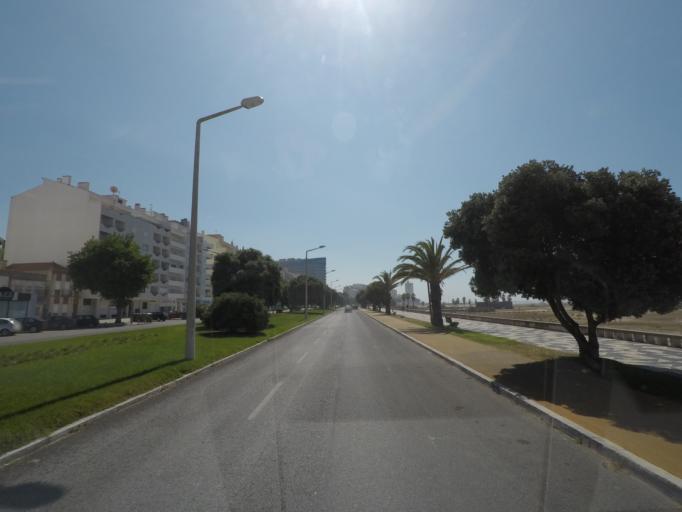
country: PT
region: Coimbra
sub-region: Figueira da Foz
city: Buarcos
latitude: 40.1589
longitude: -8.8697
